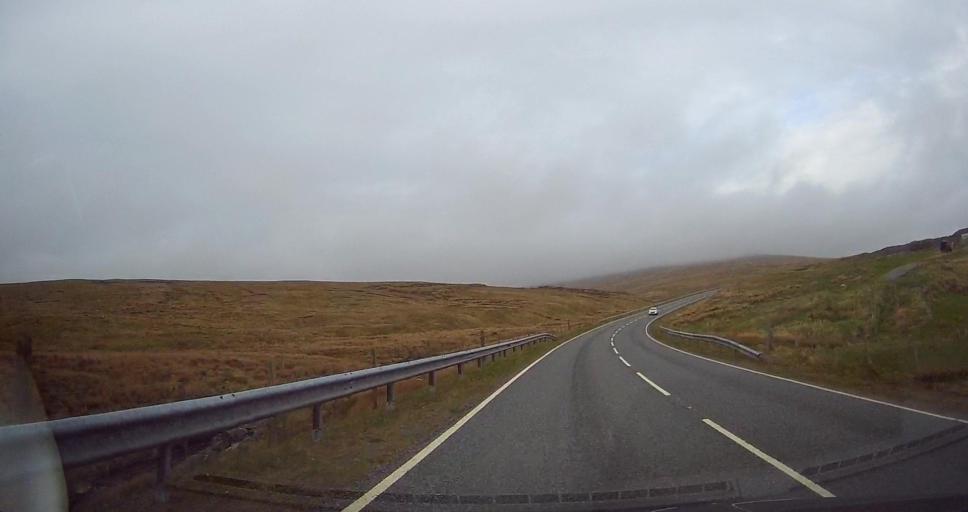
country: GB
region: Scotland
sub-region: Shetland Islands
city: Sandwick
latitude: 60.0032
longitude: -1.2796
